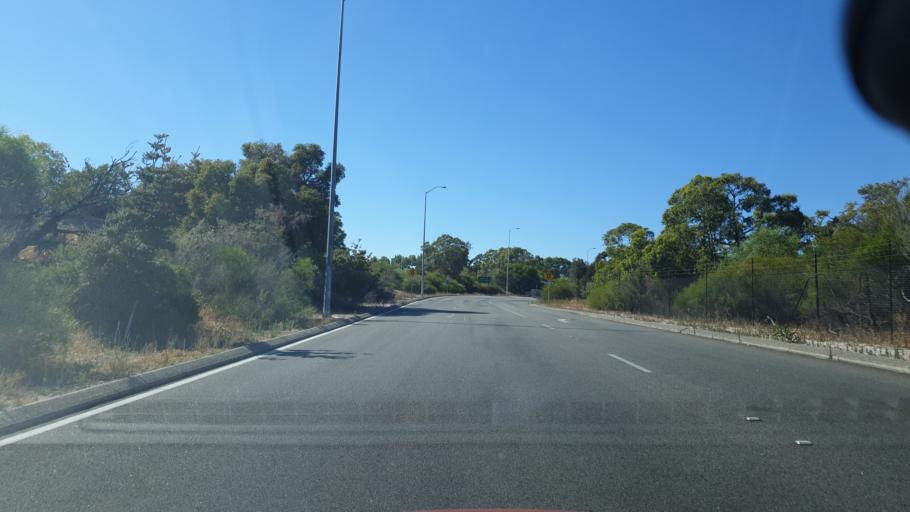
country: AU
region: Western Australia
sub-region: Melville
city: Mount Pleasant
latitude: -32.0446
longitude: 115.8557
